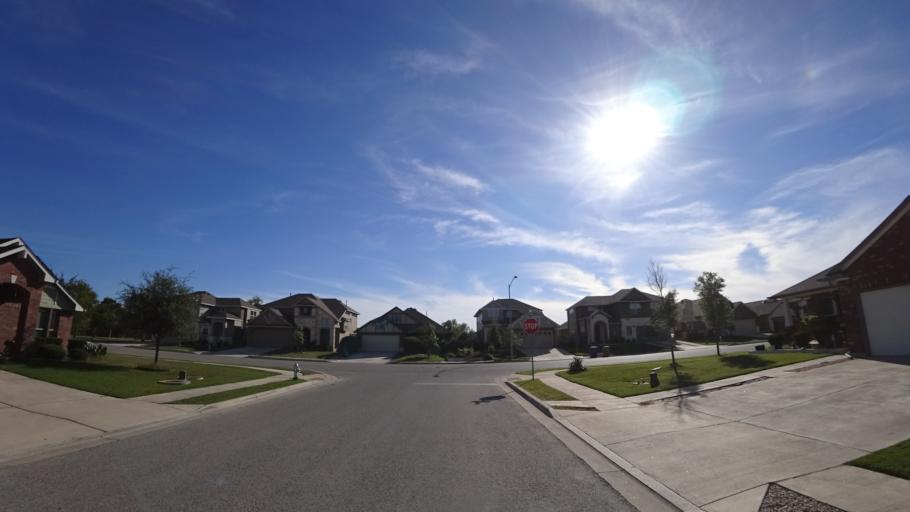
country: US
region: Texas
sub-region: Travis County
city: Austin
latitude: 30.2604
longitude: -97.6719
